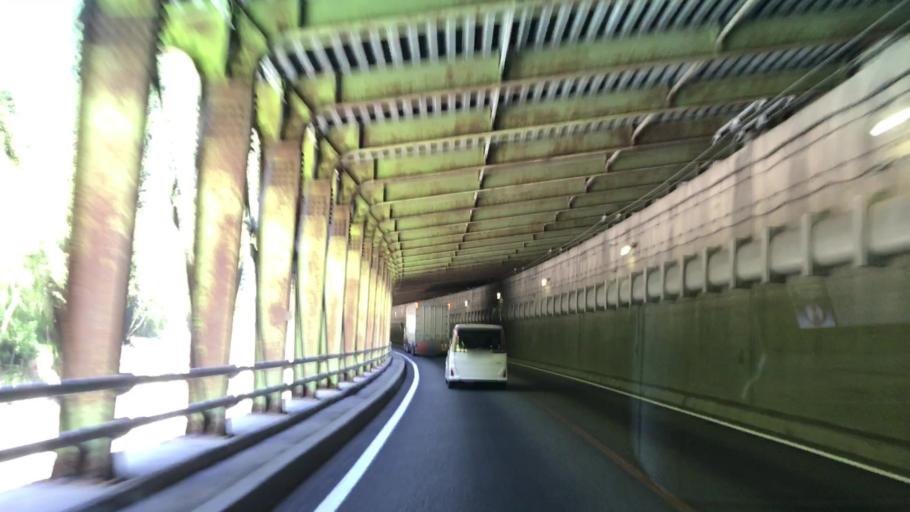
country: JP
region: Hokkaido
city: Shimo-furano
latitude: 42.9414
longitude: 142.6006
